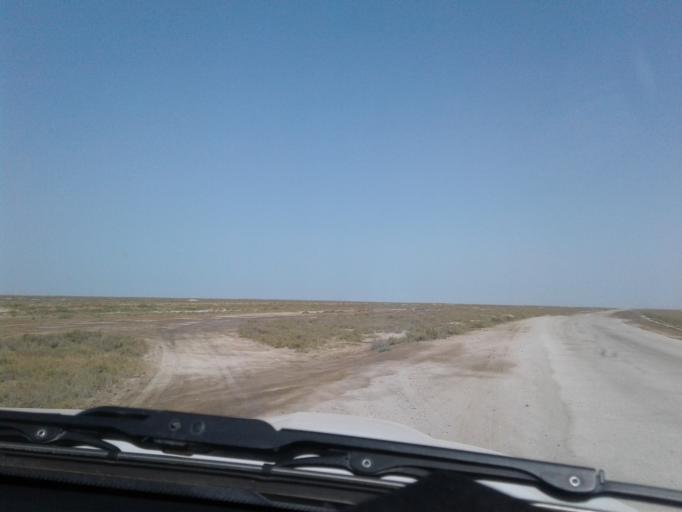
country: IR
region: Golestan
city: Gomishan
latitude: 37.8433
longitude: 53.8859
